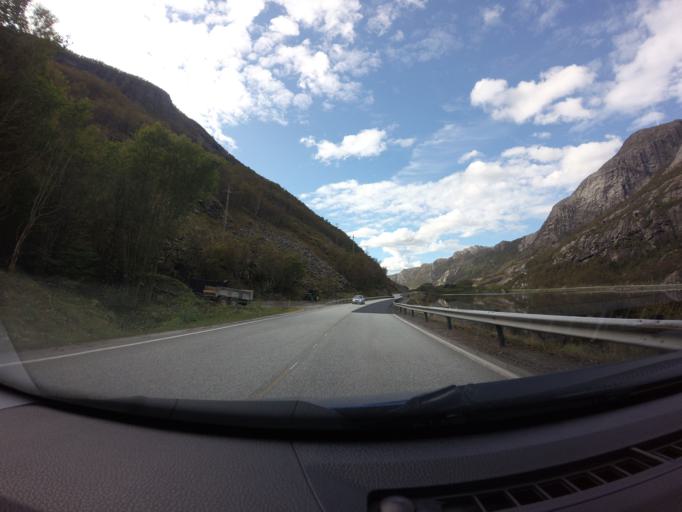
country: NO
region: Rogaland
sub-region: Forsand
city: Forsand
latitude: 58.8328
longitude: 6.1073
